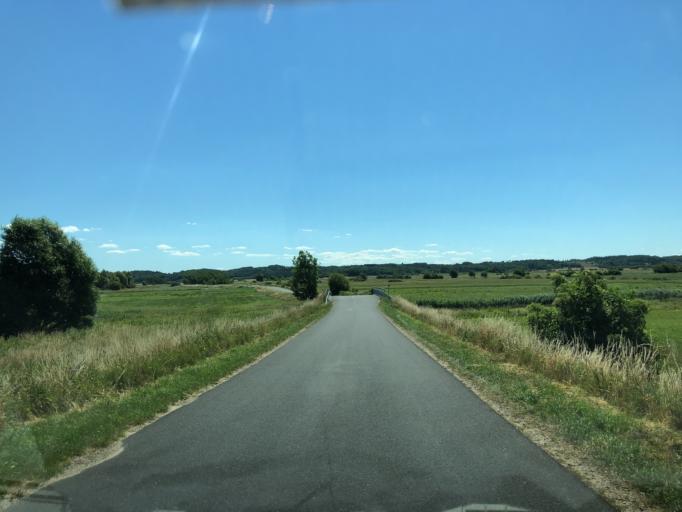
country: DK
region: Central Jutland
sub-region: Viborg Kommune
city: Viborg
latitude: 56.5533
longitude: 9.4265
